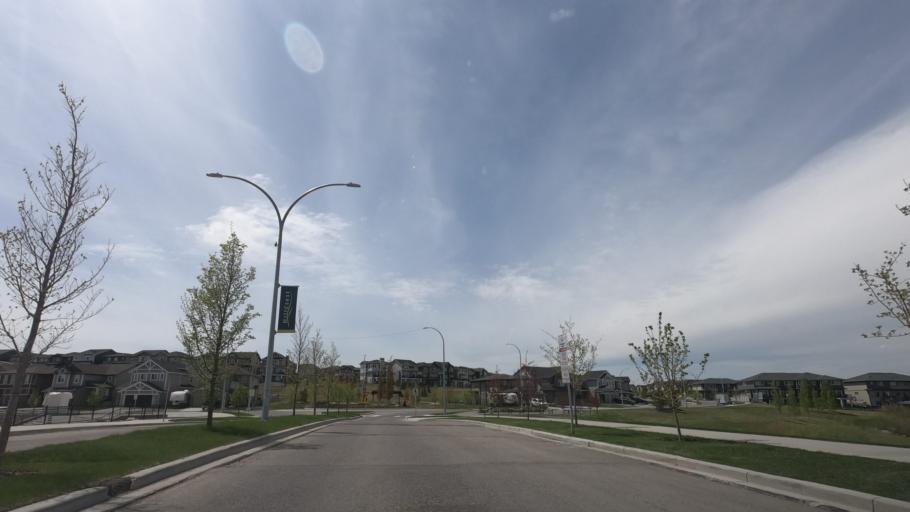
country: CA
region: Alberta
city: Airdrie
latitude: 51.2542
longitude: -114.0144
